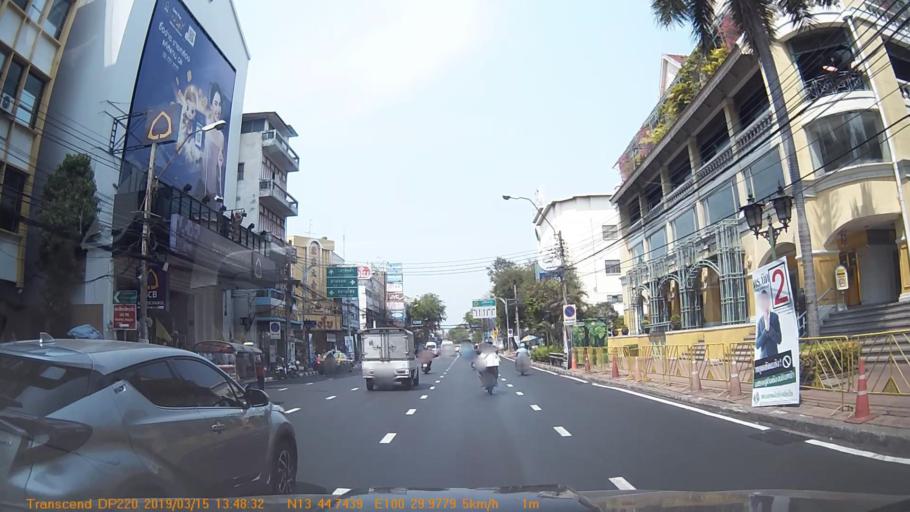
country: TH
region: Bangkok
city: Bangkok
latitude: 13.7457
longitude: 100.4996
